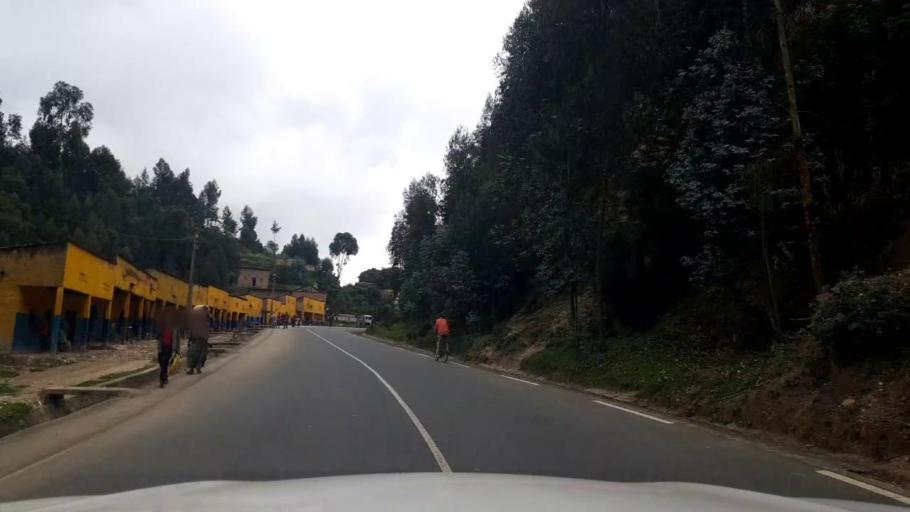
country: RW
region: Northern Province
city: Musanze
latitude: -1.6517
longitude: 29.5087
